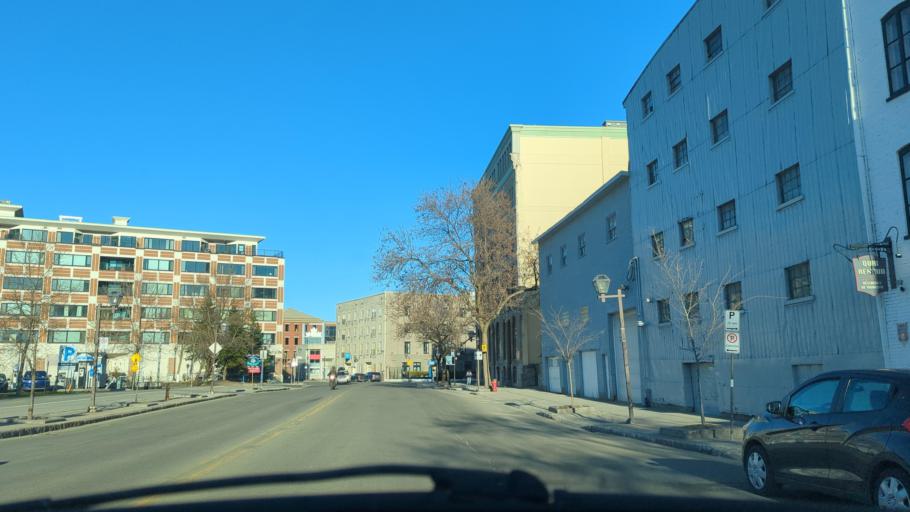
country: CA
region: Quebec
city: Quebec
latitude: 46.8169
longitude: -71.2050
